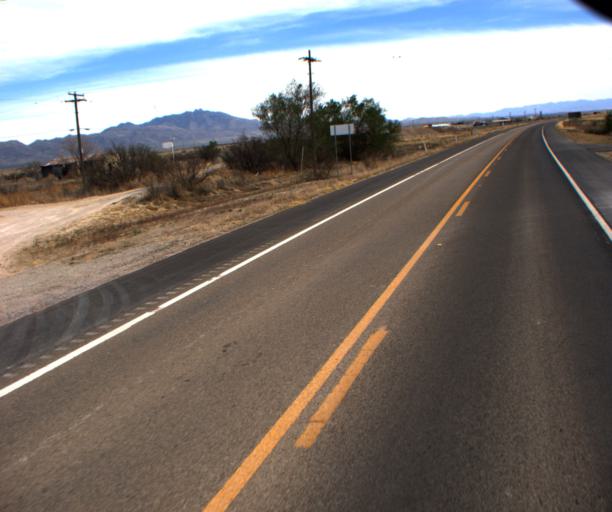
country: US
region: Arizona
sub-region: Cochise County
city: Willcox
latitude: 32.2466
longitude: -109.8208
